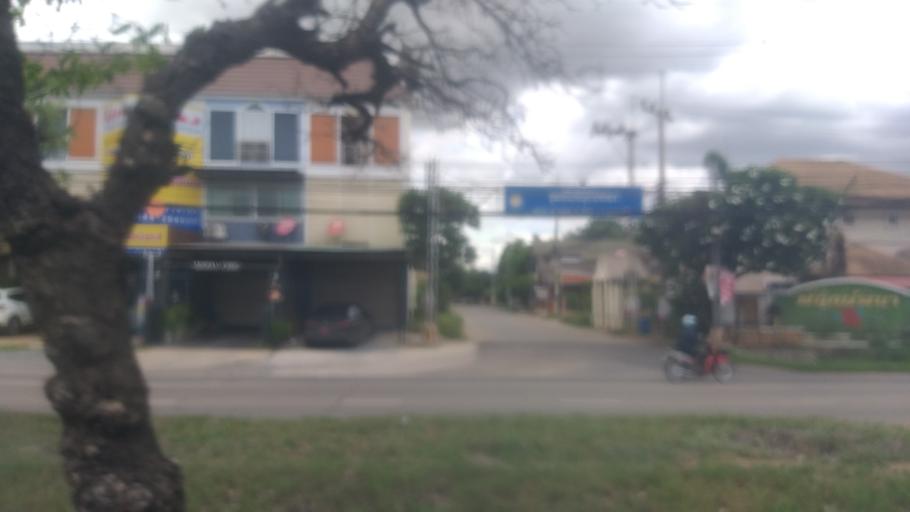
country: TH
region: Nakhon Ratchasima
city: Nakhon Ratchasima
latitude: 15.0470
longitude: 102.1318
